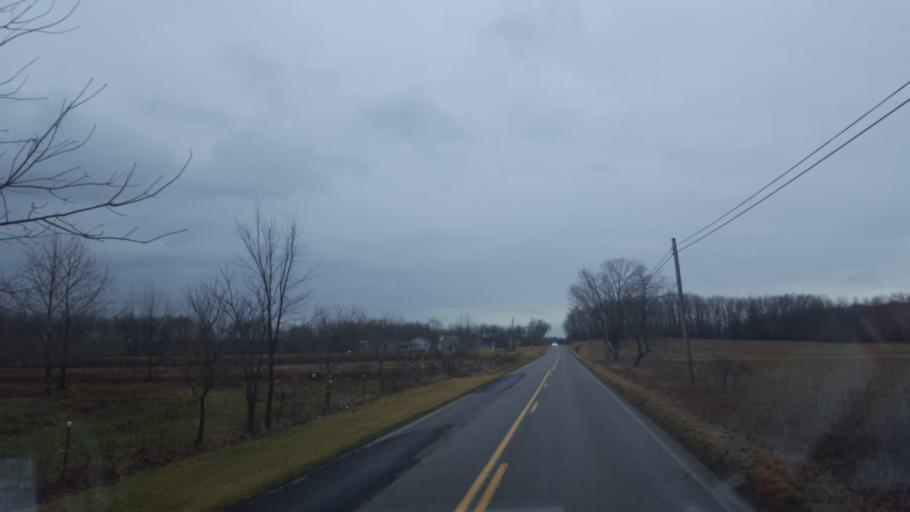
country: US
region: Ohio
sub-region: Knox County
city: Fredericktown
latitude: 40.4630
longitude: -82.5228
